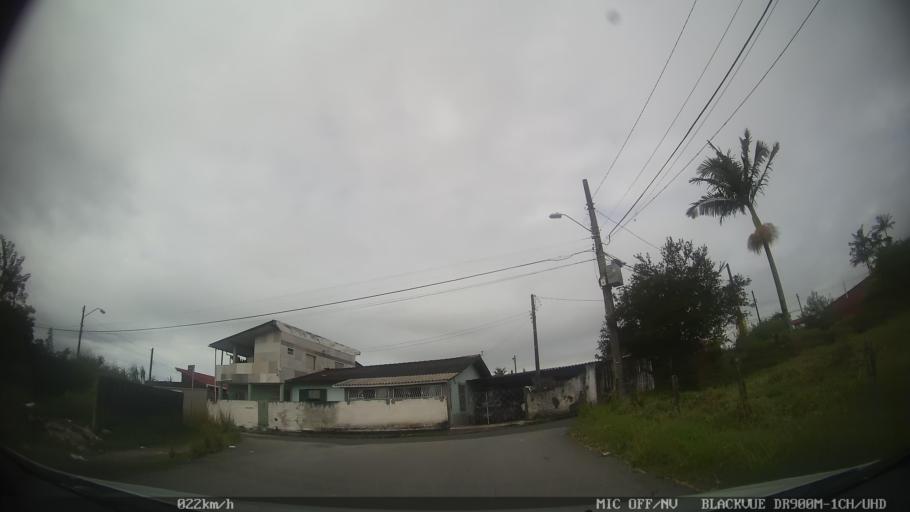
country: BR
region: Santa Catarina
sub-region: Biguacu
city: Biguacu
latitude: -27.5380
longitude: -48.6363
